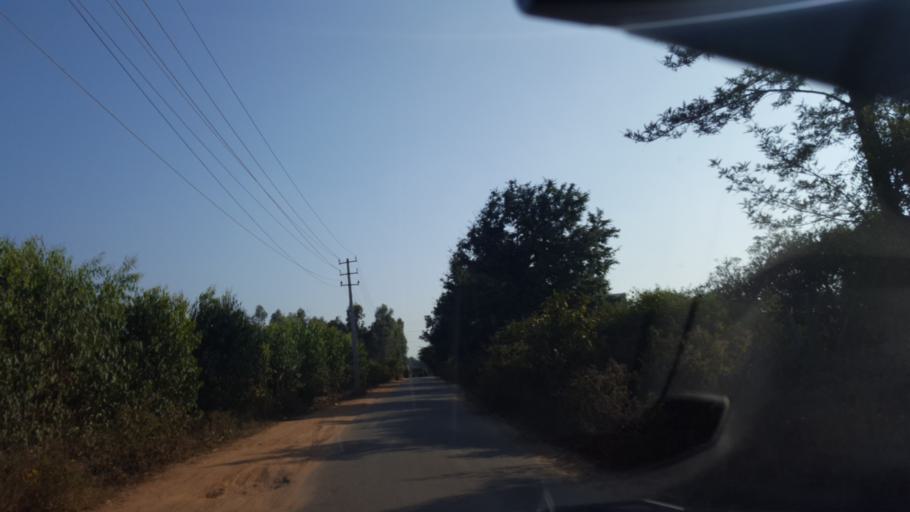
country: IN
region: Karnataka
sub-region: Bangalore Rural
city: Hoskote
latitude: 12.9222
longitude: 77.7568
